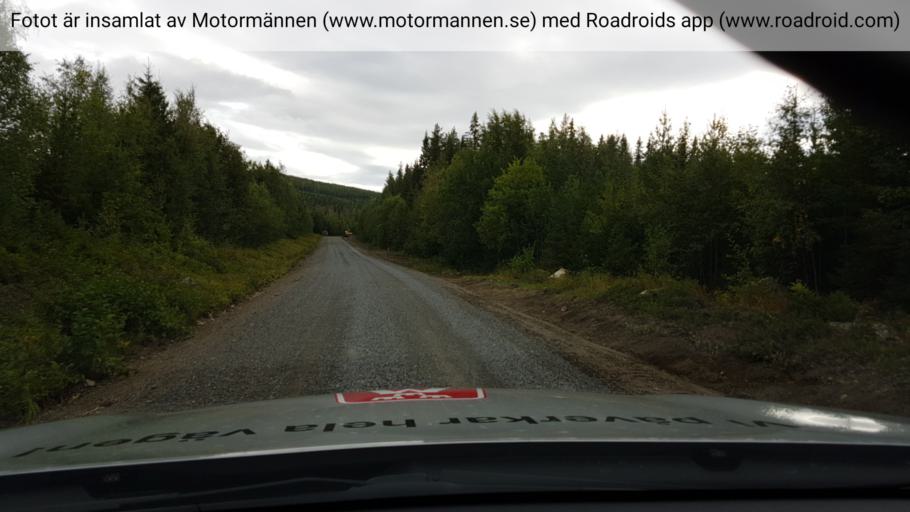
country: SE
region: Jaemtland
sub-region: Ragunda Kommun
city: Hammarstrand
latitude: 62.8753
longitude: 16.0578
